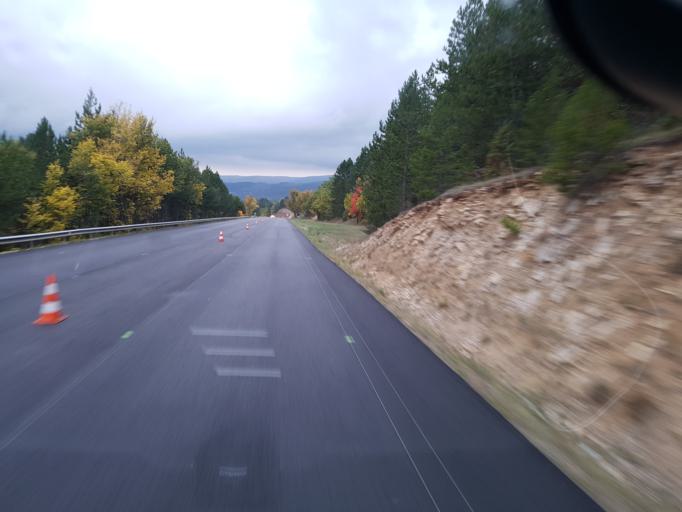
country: FR
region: Languedoc-Roussillon
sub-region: Departement de la Lozere
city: Mende
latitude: 44.5355
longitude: 3.5988
